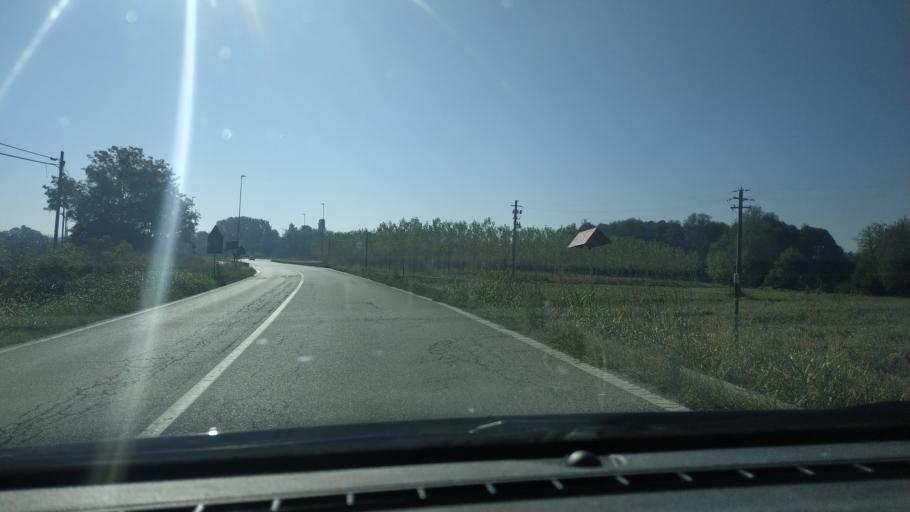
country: IT
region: Piedmont
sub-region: Provincia di Torino
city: Verolengo
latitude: 45.1914
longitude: 7.9512
